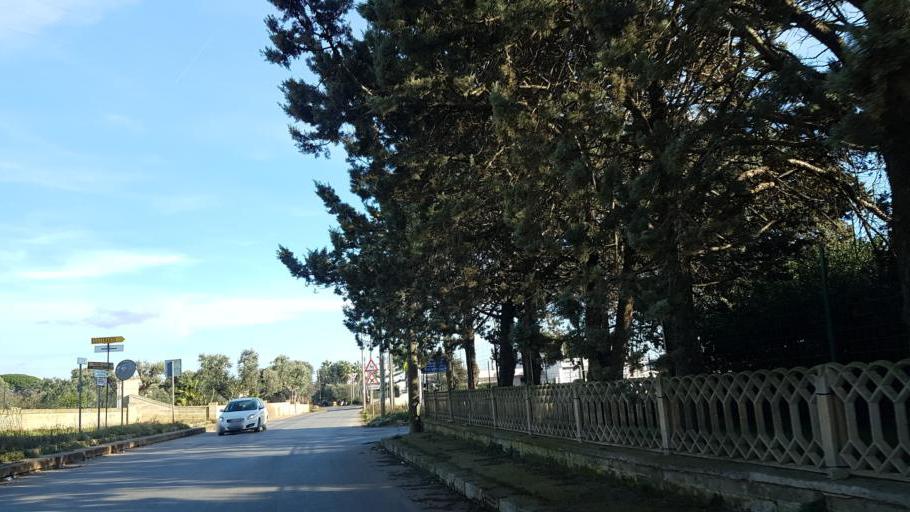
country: IT
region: Apulia
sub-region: Provincia di Brindisi
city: Carovigno
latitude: 40.7024
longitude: 17.6688
